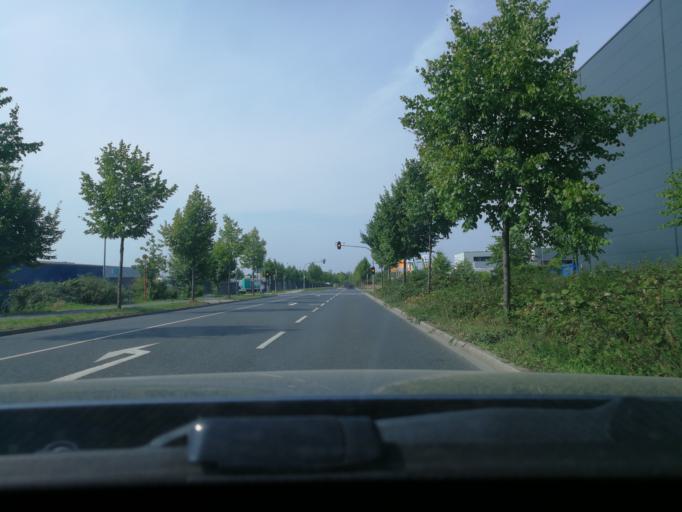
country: DE
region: North Rhine-Westphalia
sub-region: Regierungsbezirk Dusseldorf
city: Dusseldorf
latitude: 51.1553
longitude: 6.7635
